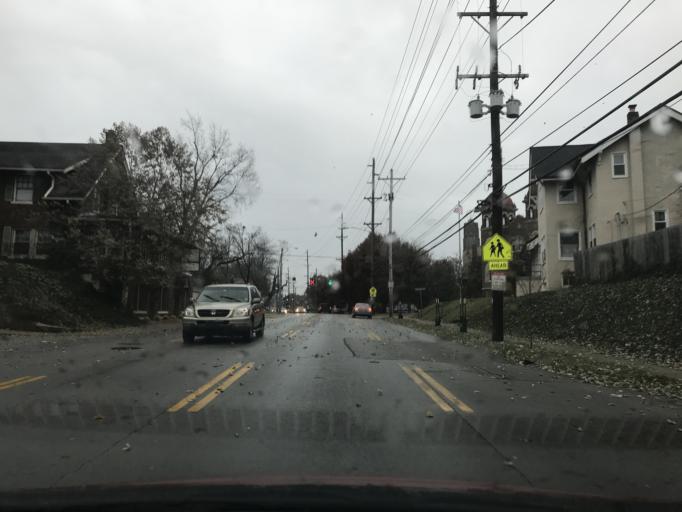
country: US
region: Kentucky
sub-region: Jefferson County
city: Audubon Park
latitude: 38.2268
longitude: -85.6985
